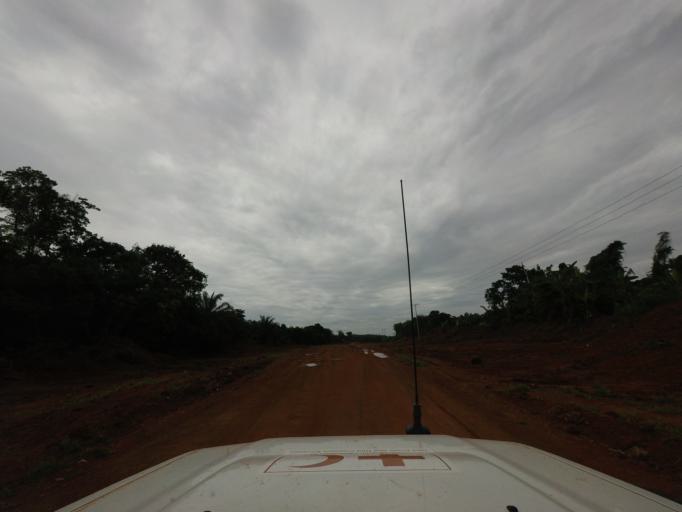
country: LR
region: Nimba
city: Sanniquellie
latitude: 7.2316
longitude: -8.9101
